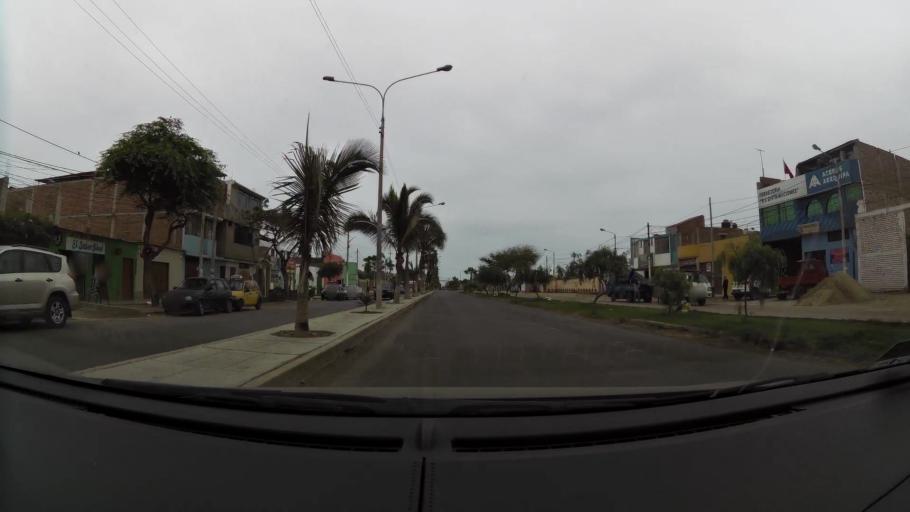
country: PE
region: La Libertad
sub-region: Provincia de Trujillo
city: Buenos Aires
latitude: -8.1379
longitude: -79.0501
